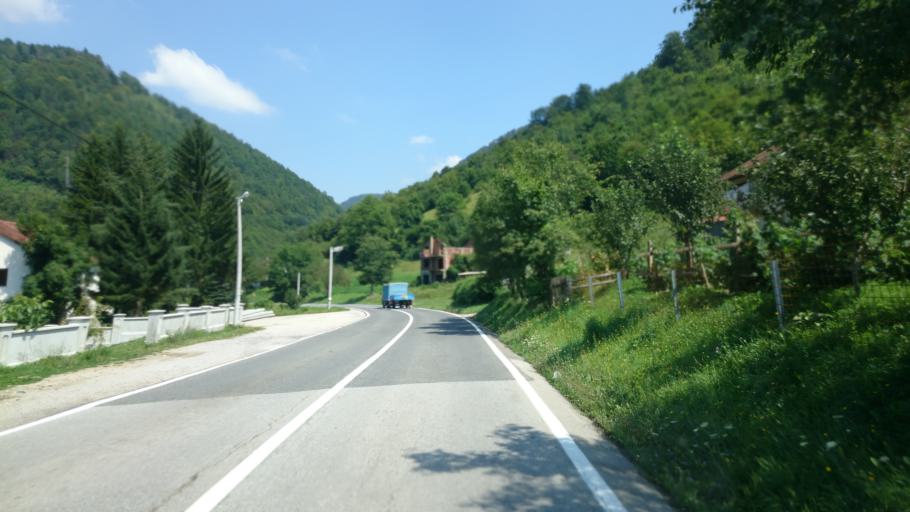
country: BA
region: Federation of Bosnia and Herzegovina
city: Donji Vakuf
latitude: 44.2006
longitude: 17.3393
